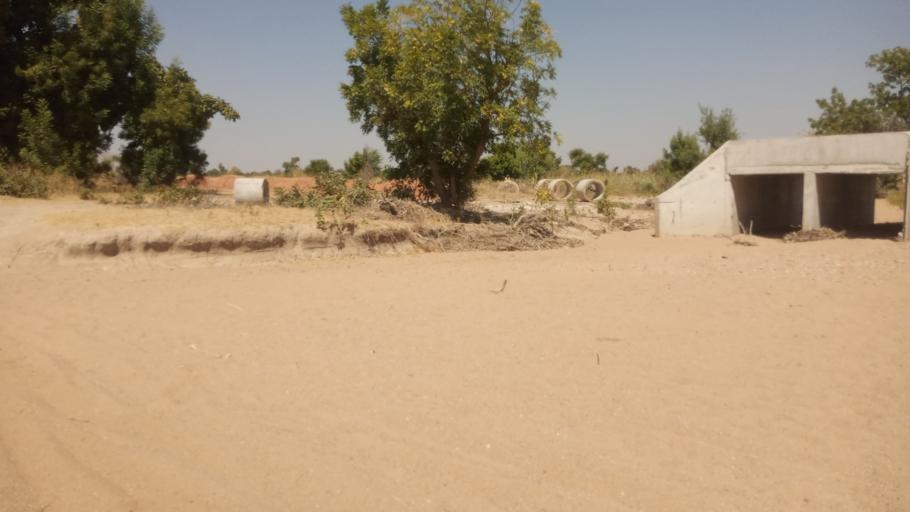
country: NG
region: Adamawa
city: Mayo Belwa
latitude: 9.0926
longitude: 12.0247
